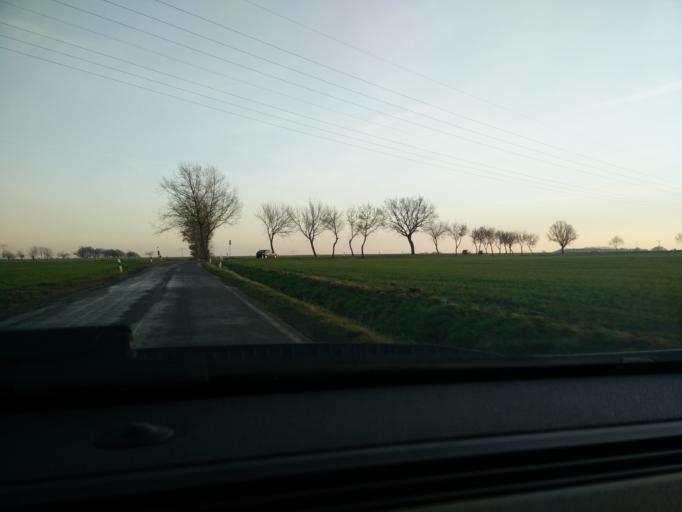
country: DE
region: Saxony
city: Kitzscher
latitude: 51.1864
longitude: 12.5333
